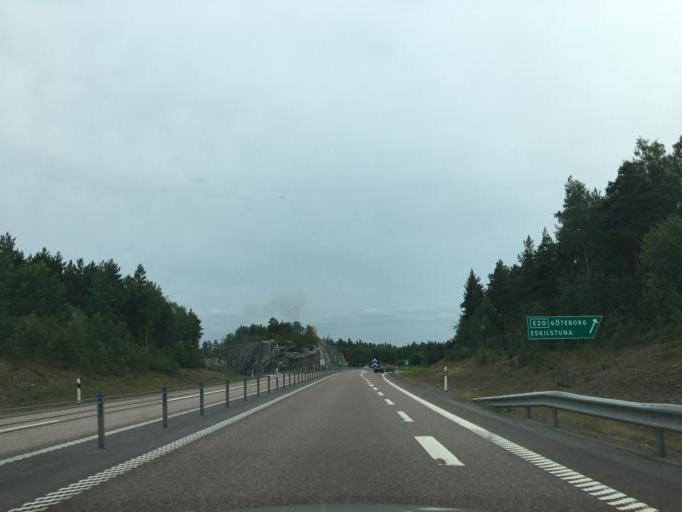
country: SE
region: Soedermanland
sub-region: Strangnas Kommun
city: Strangnas
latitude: 59.3703
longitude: 16.9587
